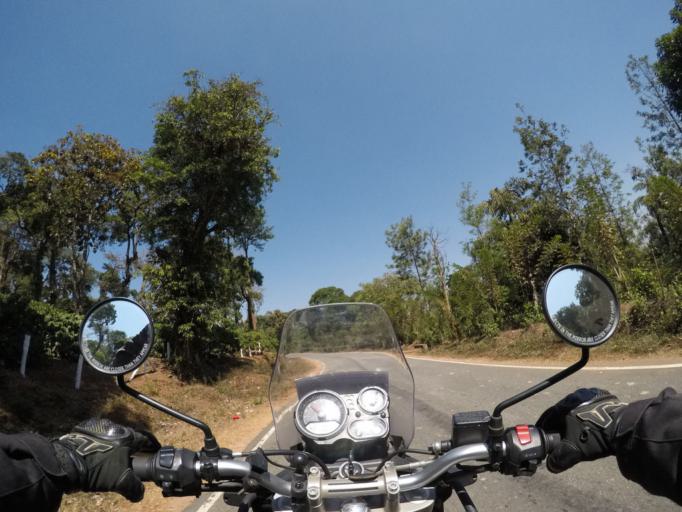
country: IN
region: Karnataka
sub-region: Hassan
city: Sakleshpur
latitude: 13.0101
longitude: 75.6997
